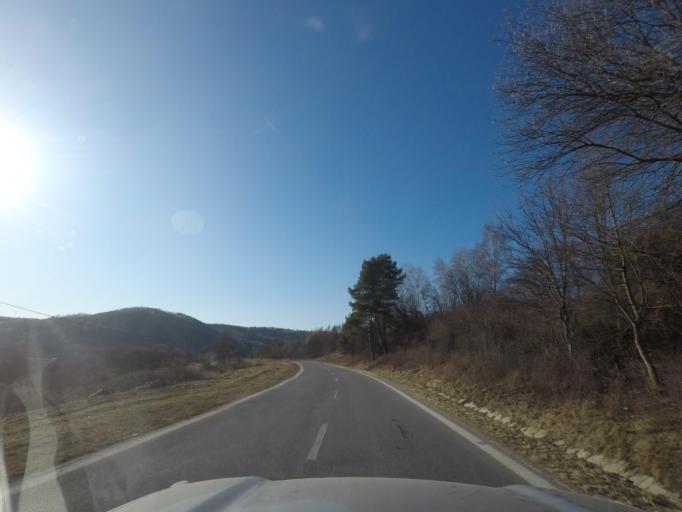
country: SK
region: Presovsky
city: Medzilaborce
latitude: 49.2515
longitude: 21.9208
